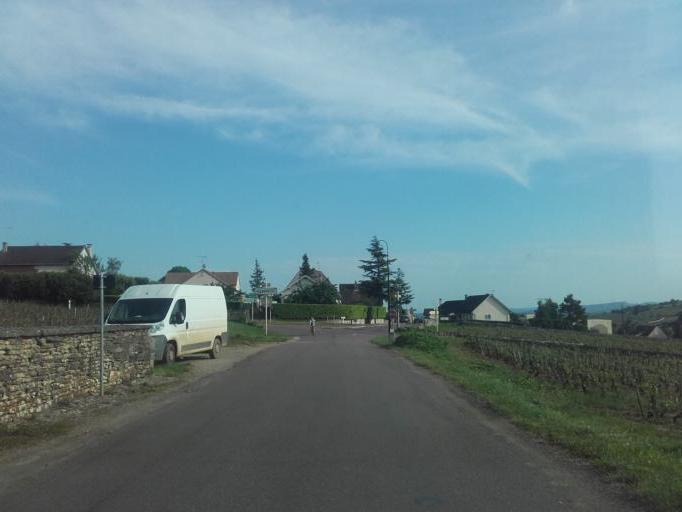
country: FR
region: Bourgogne
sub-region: Departement de la Cote-d'Or
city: Meursault
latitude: 46.9893
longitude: 4.7668
